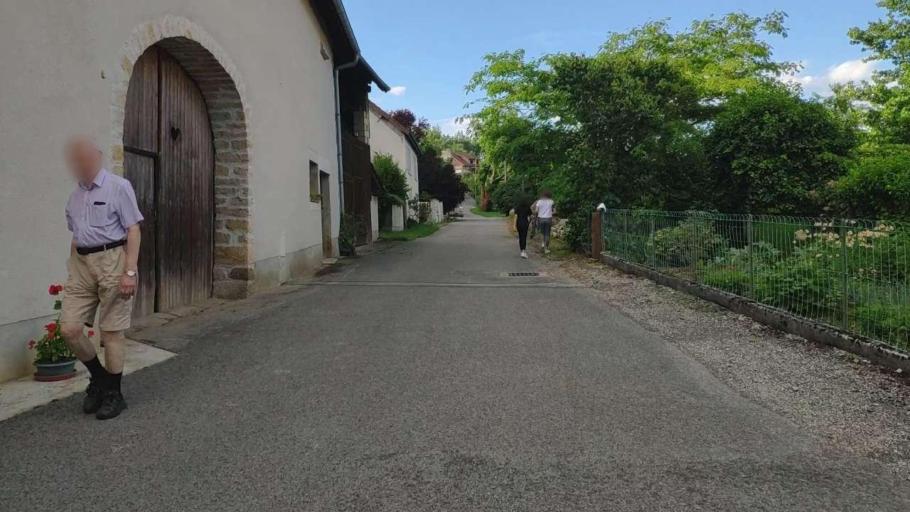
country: FR
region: Franche-Comte
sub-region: Departement du Jura
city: Bletterans
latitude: 46.7626
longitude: 5.5271
